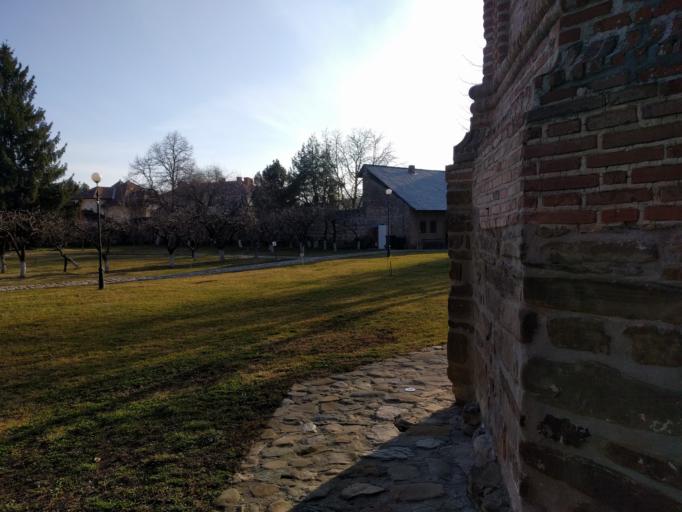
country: RO
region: Dambovita
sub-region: Municipiul Targoviste
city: Targoviste
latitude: 44.9318
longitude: 25.4591
